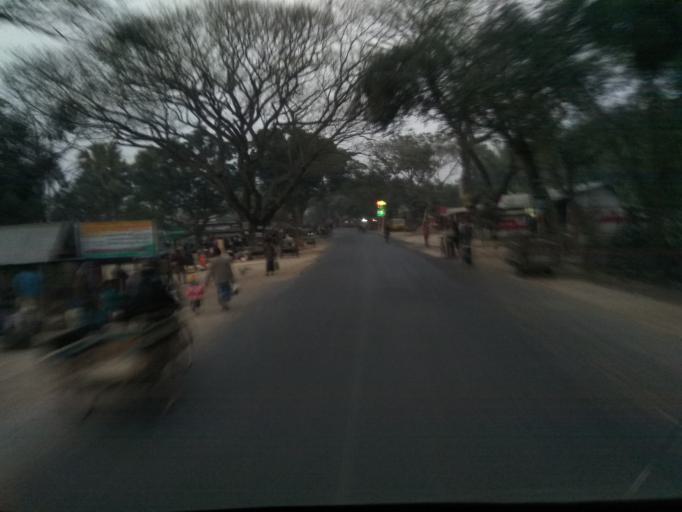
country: BD
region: Rajshahi
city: Bogra
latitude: 24.7511
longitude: 89.3433
